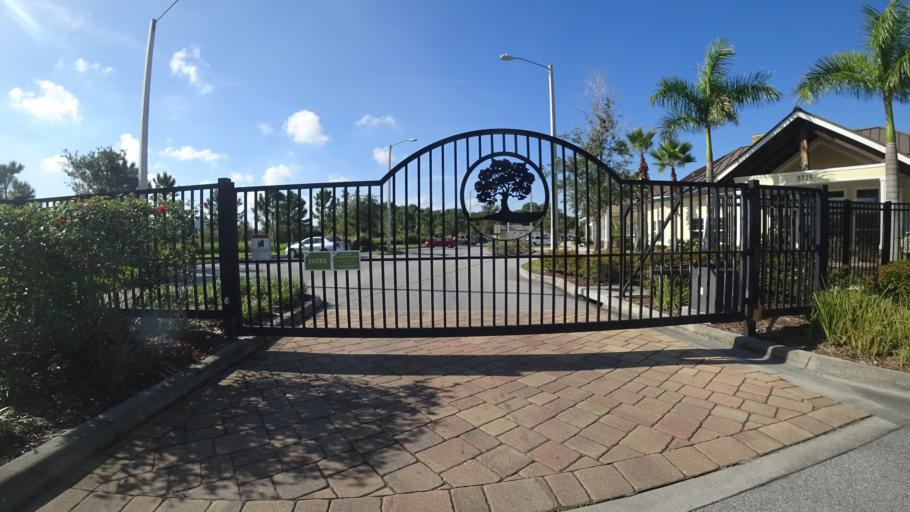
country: US
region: Florida
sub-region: Manatee County
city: Ellenton
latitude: 27.4967
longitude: -82.4875
